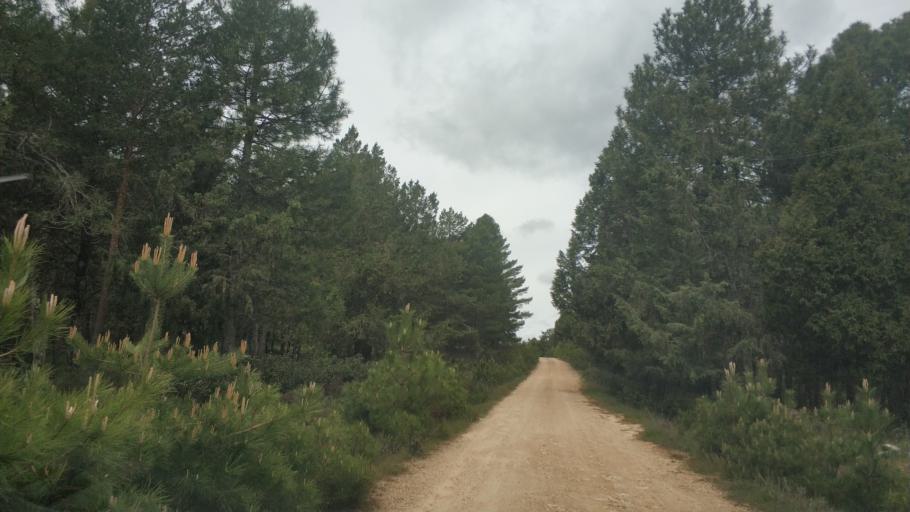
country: ES
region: Castille and Leon
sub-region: Provincia de Soria
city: Casarejos
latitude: 41.7730
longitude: -3.0385
